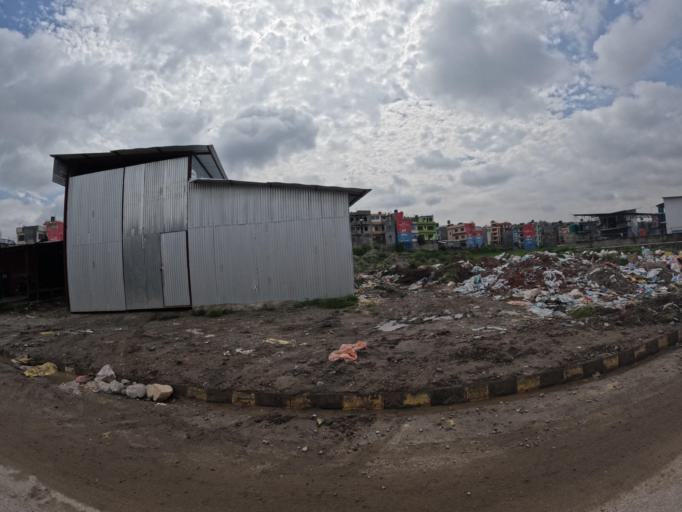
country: NP
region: Central Region
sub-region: Bagmati Zone
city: Kathmandu
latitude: 27.7605
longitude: 85.3165
